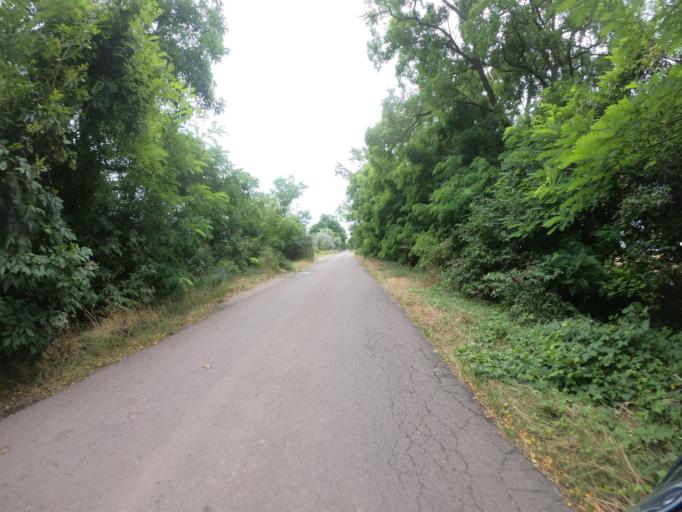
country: HU
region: Borsod-Abauj-Zemplen
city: Szentistvan
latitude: 47.7342
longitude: 20.6832
